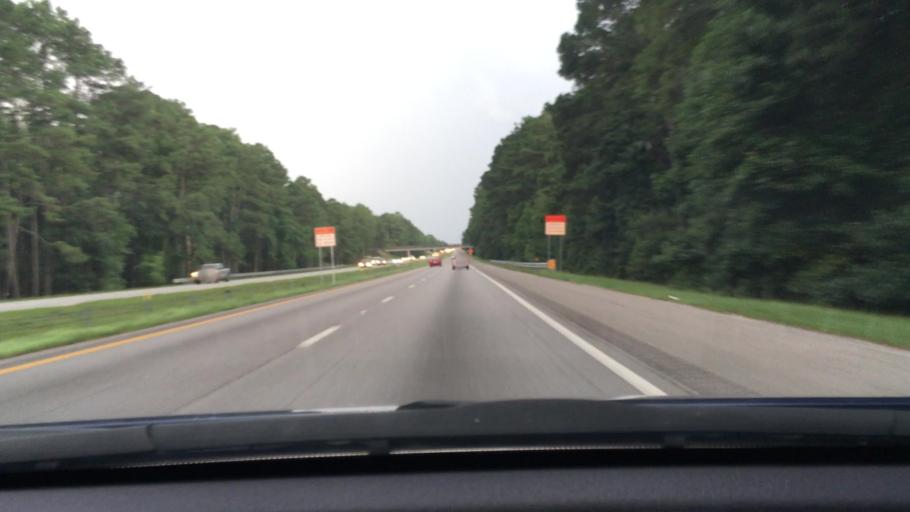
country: US
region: South Carolina
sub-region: Kershaw County
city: Elgin
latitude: 34.1301
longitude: -80.7732
